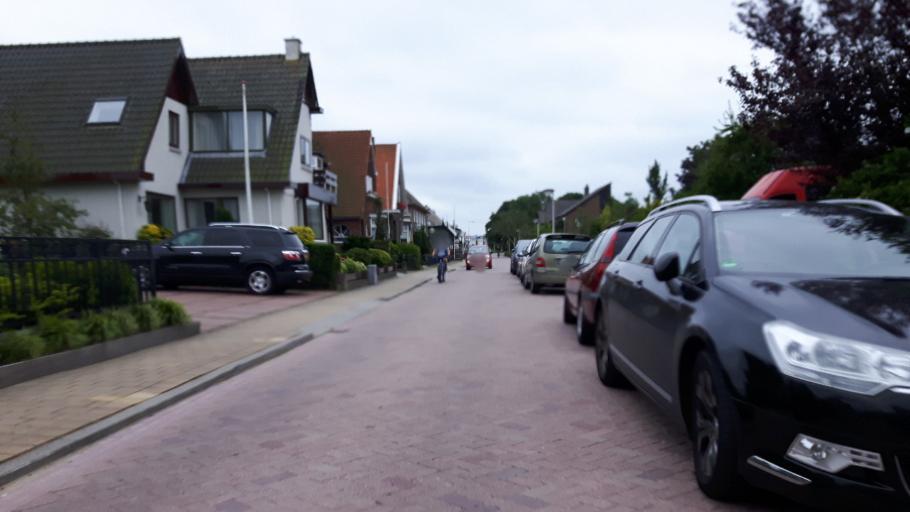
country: NL
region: South Holland
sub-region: Gemeente Kaag en Braassem
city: Oude Wetering
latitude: 52.2066
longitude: 4.6471
